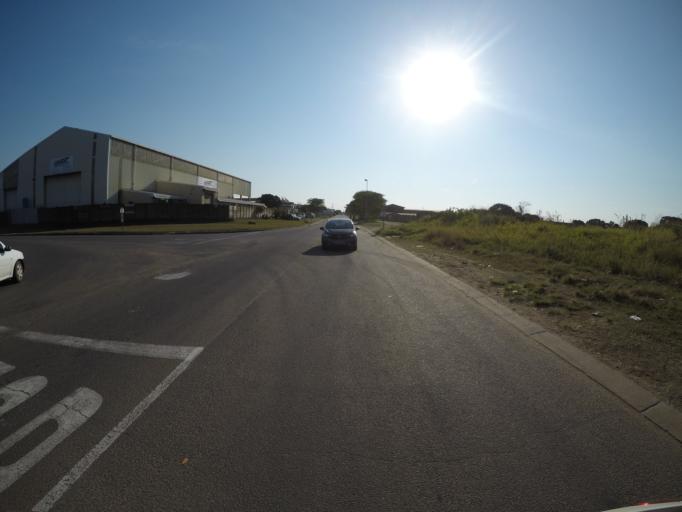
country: ZA
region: KwaZulu-Natal
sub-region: uThungulu District Municipality
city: Richards Bay
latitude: -28.7442
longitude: 32.0359
